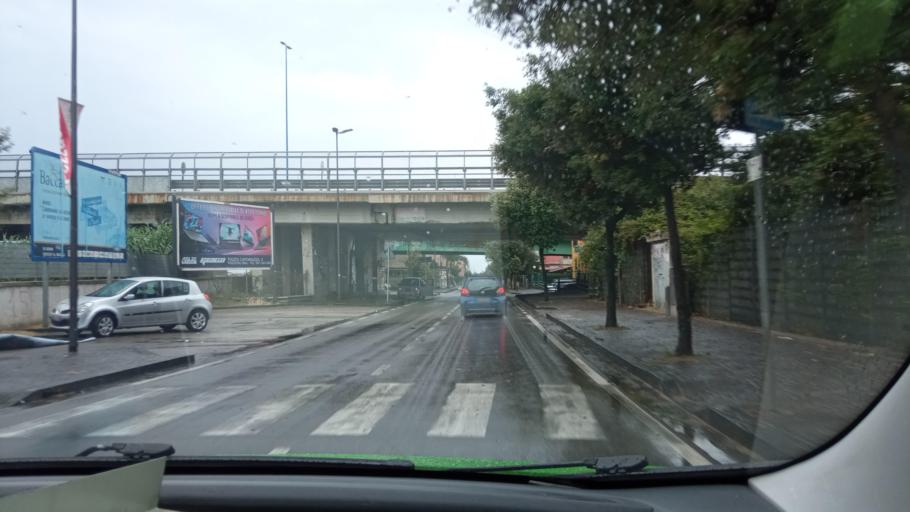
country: IT
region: Campania
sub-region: Provincia di Napoli
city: Pozzuoli
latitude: 40.8396
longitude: 14.1166
